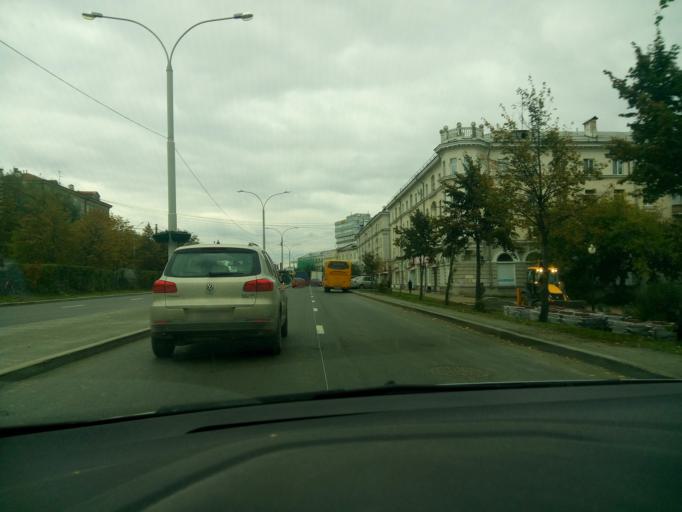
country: RU
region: Sverdlovsk
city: Yekaterinburg
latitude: 56.8391
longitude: 60.5730
